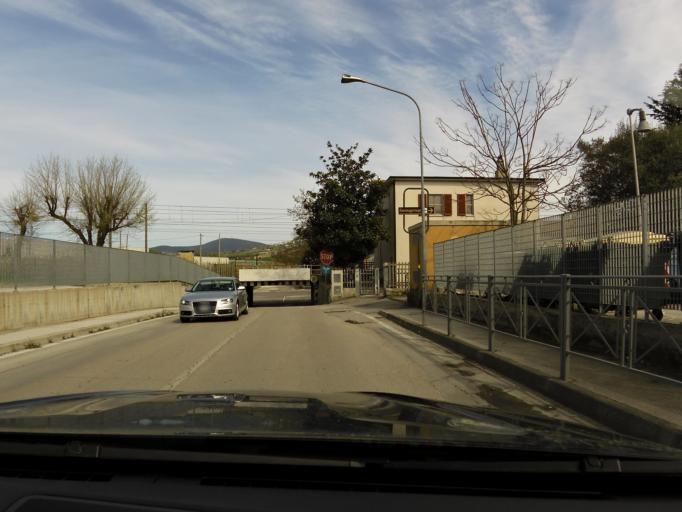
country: IT
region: The Marches
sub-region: Provincia di Ancona
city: San Biagio
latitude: 43.5280
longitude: 13.5206
